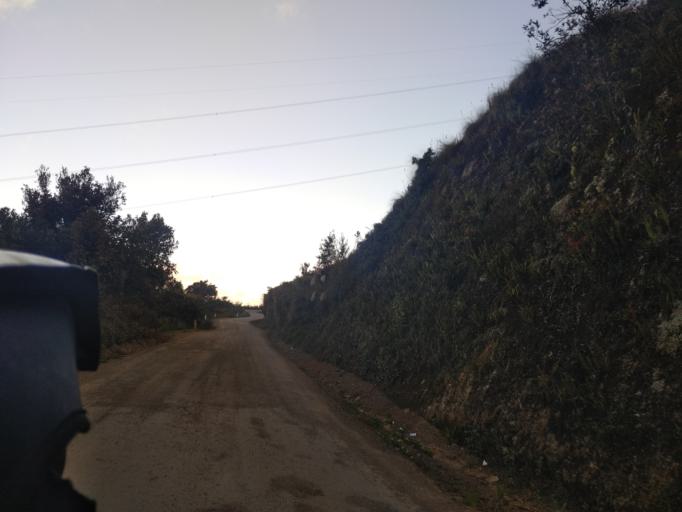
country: PE
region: Amazonas
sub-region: Provincia de Chachapoyas
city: Montevideo
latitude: -6.7174
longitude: -77.8741
